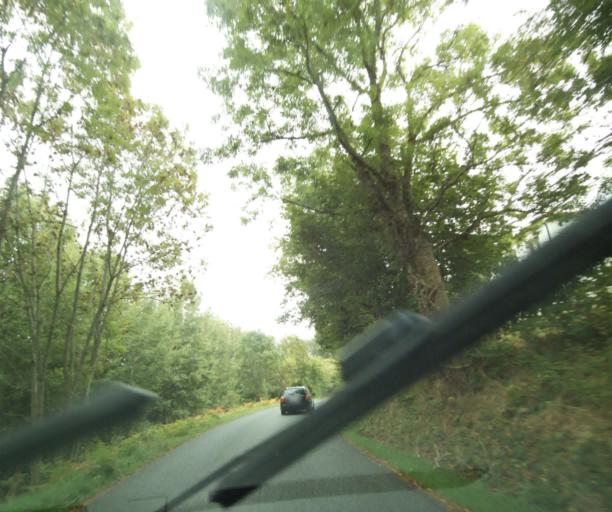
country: FR
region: Auvergne
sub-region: Departement du Puy-de-Dome
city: Orcines
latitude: 45.8007
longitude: 3.0286
